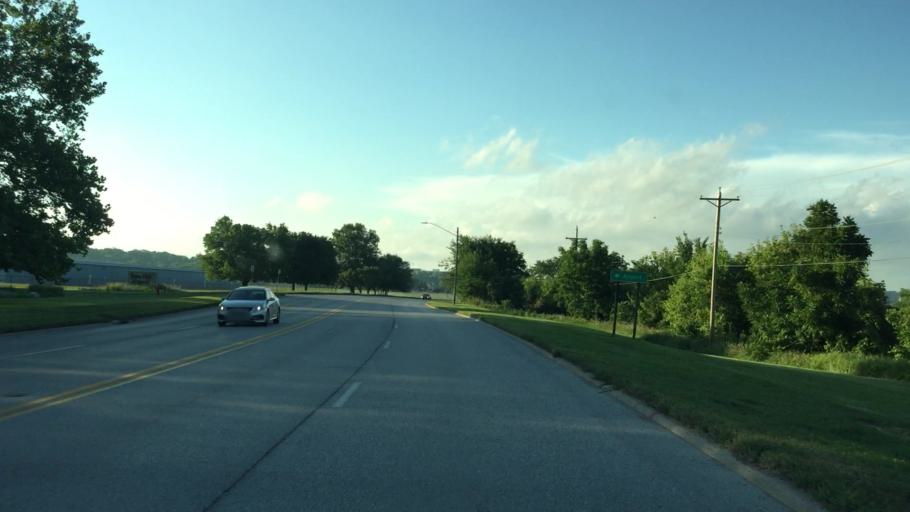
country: US
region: Iowa
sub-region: Johnson County
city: Iowa City
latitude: 41.6390
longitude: -91.5386
